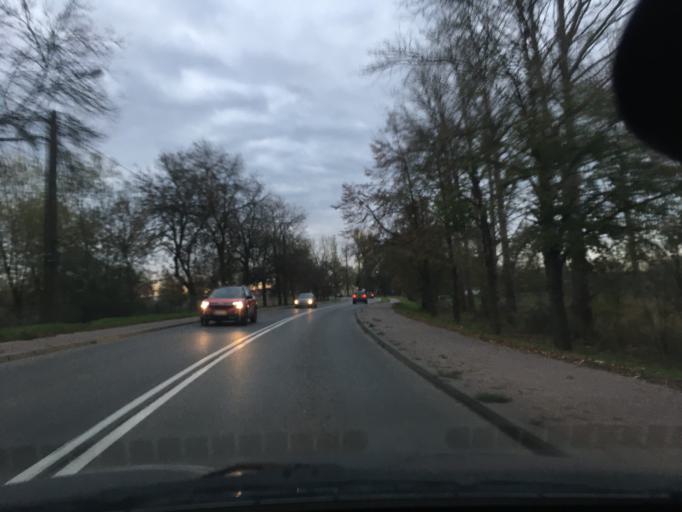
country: PL
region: Masovian Voivodeship
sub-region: Powiat piaseczynski
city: Lesznowola
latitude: 52.0902
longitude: 20.9351
